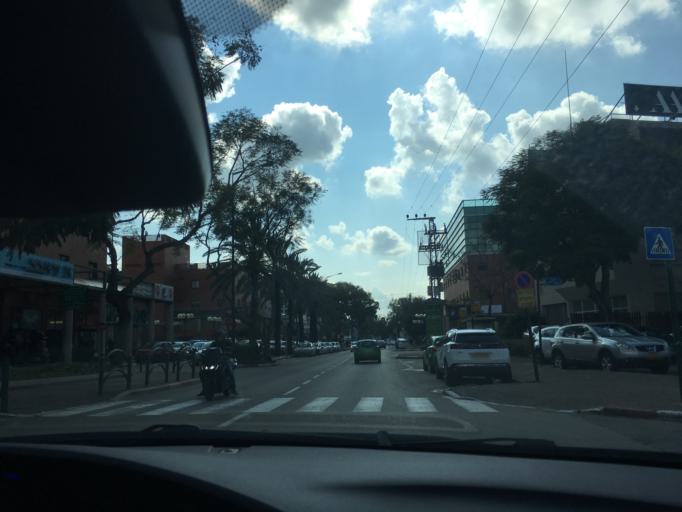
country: IL
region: Central District
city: Kfar Saba
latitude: 32.1781
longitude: 34.9278
